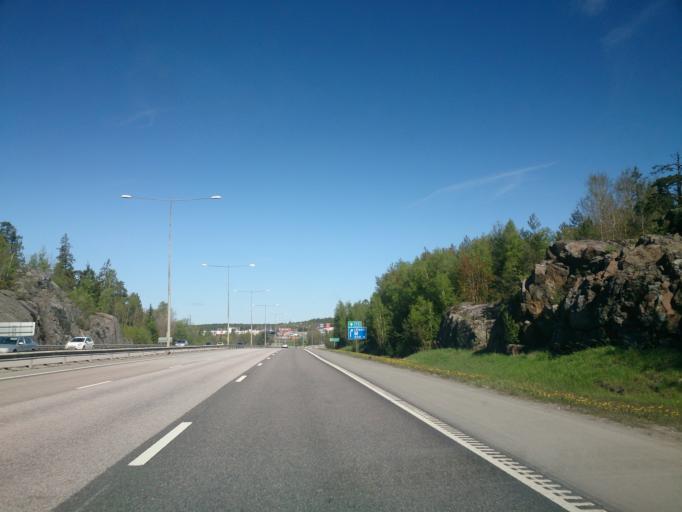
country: SE
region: Stockholm
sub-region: Haninge Kommun
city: Handen
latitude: 59.1944
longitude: 18.1383
